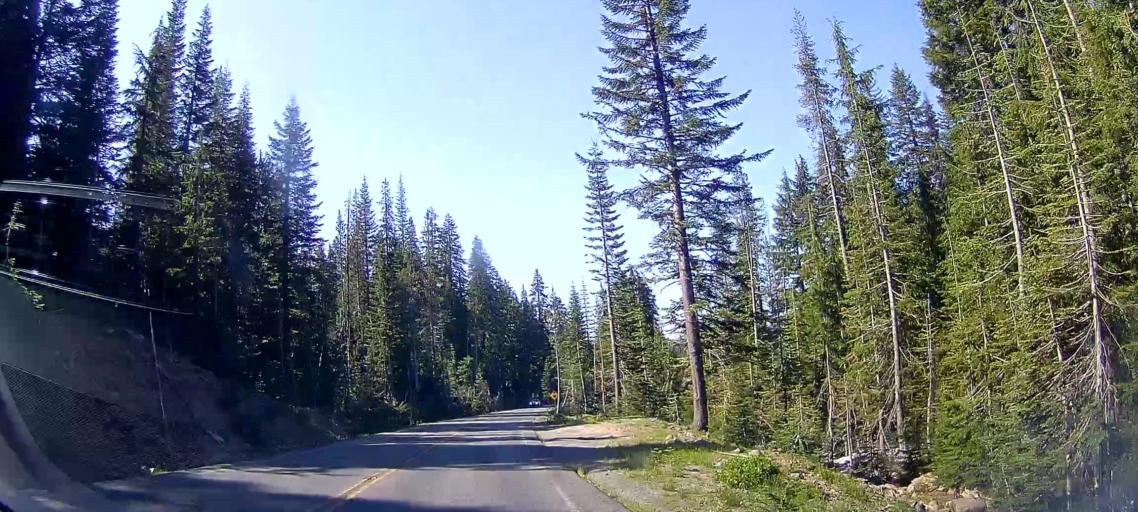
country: US
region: Oregon
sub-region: Jackson County
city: Shady Cove
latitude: 42.8985
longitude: -122.1330
